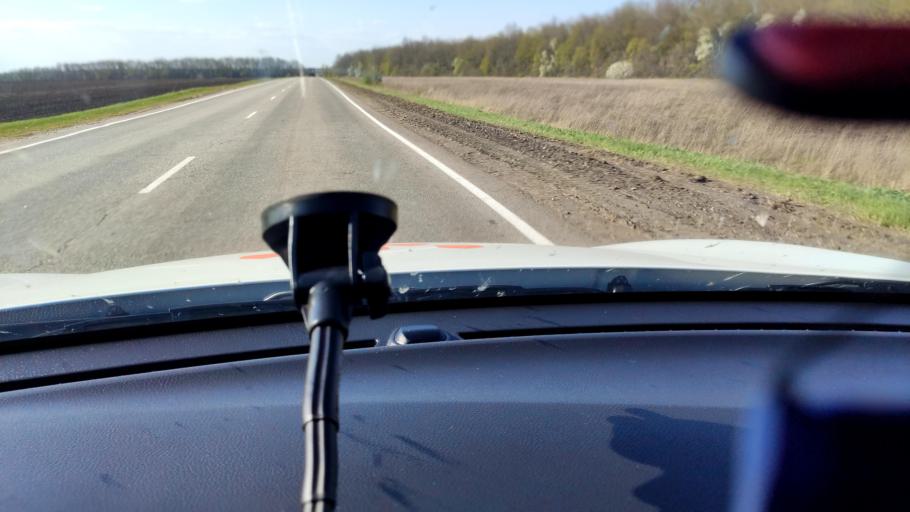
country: RU
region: Voronezj
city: Shilovo
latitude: 51.4358
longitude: 39.0016
